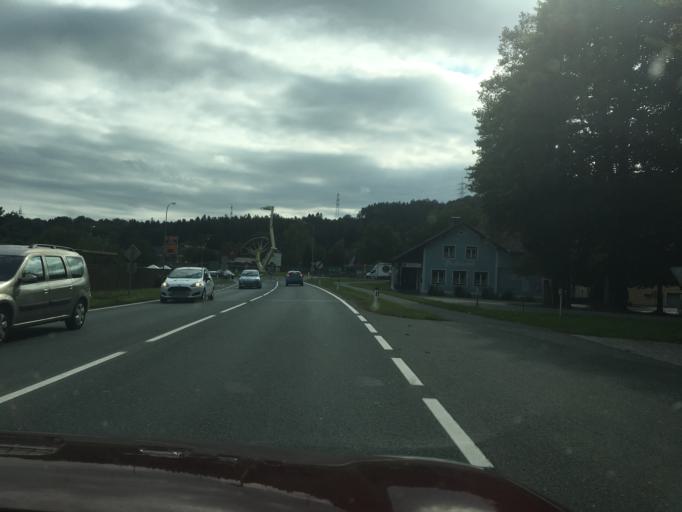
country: AT
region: Styria
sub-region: Politischer Bezirk Deutschlandsberg
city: Hollenegg
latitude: 46.8010
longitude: 15.2212
